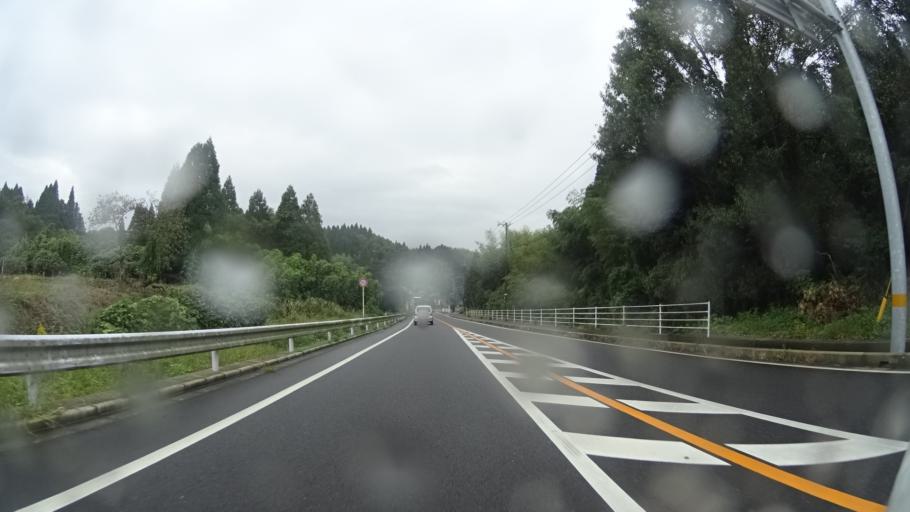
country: JP
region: Kagoshima
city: Kajiki
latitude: 31.8127
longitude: 130.6771
